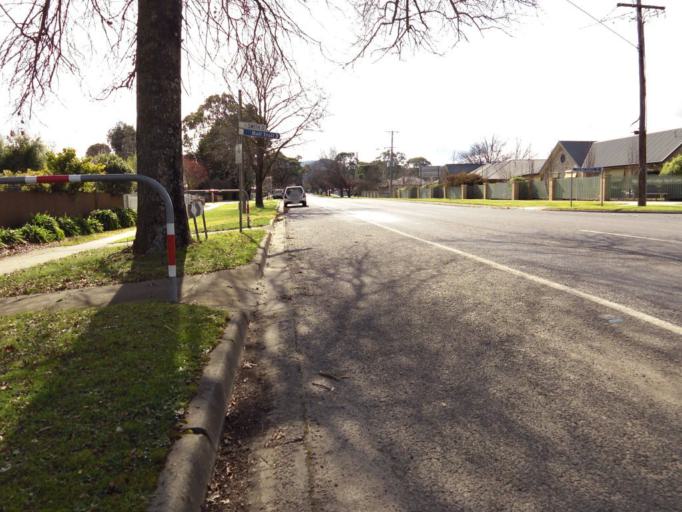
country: AU
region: Victoria
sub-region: Wangaratta
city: Wangaratta
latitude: -36.5574
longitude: 146.7205
